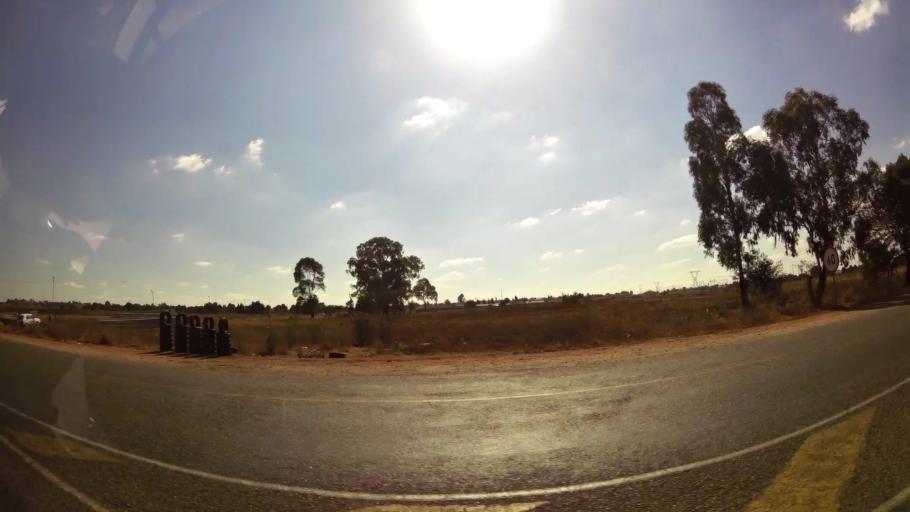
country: ZA
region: Gauteng
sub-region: West Rand District Municipality
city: Randfontein
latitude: -26.1814
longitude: 27.7502
